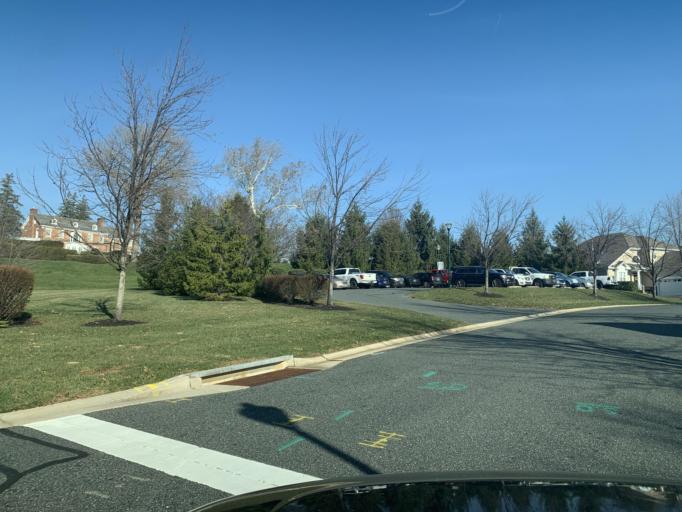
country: US
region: Maryland
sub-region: Harford County
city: Havre de Grace
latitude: 39.5489
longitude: -76.1281
